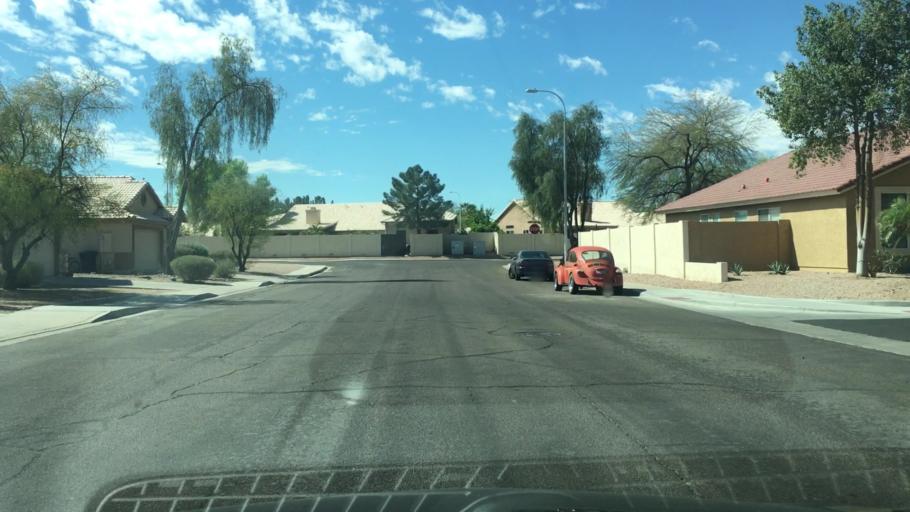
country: US
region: Arizona
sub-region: Maricopa County
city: Chandler
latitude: 33.3108
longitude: -111.8116
